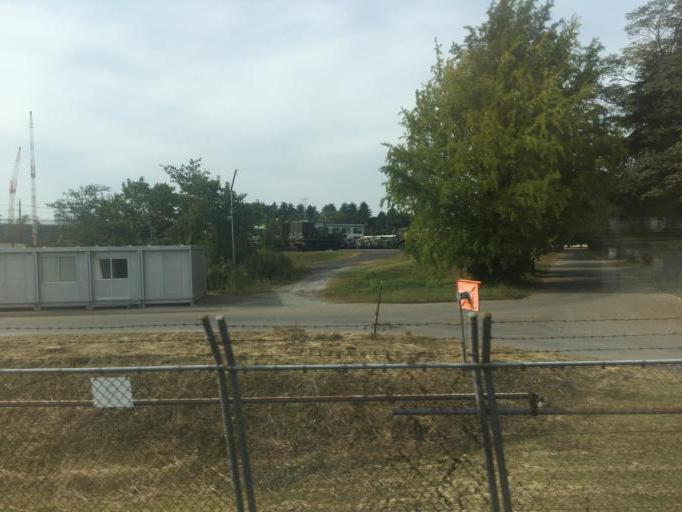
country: JP
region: Saitama
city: Sayama
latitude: 35.8402
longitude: 139.4048
